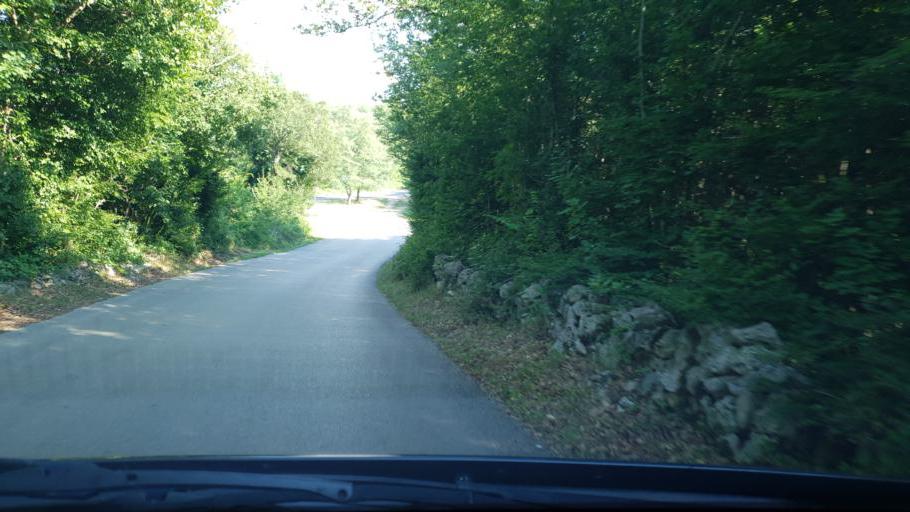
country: HR
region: Primorsko-Goranska
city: Njivice
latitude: 45.1440
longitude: 14.5820
